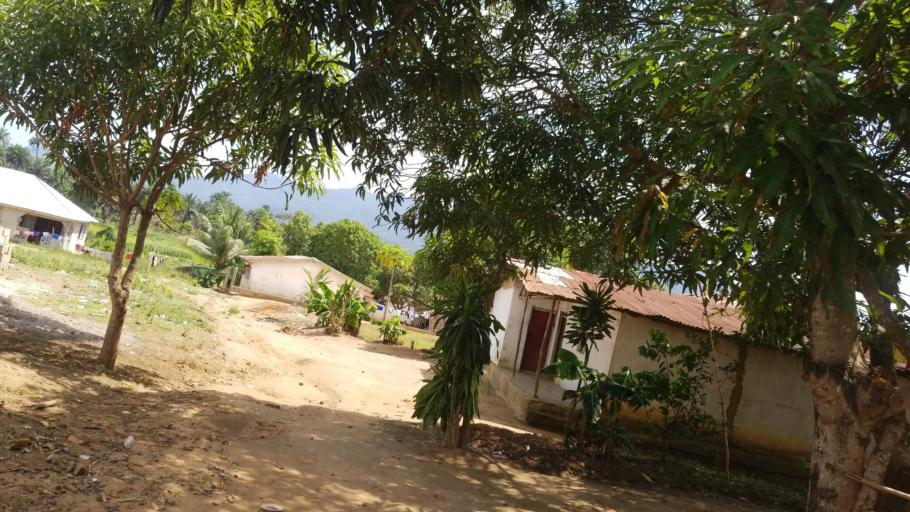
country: SL
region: Western Area
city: Waterloo
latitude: 8.3105
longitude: -13.0578
